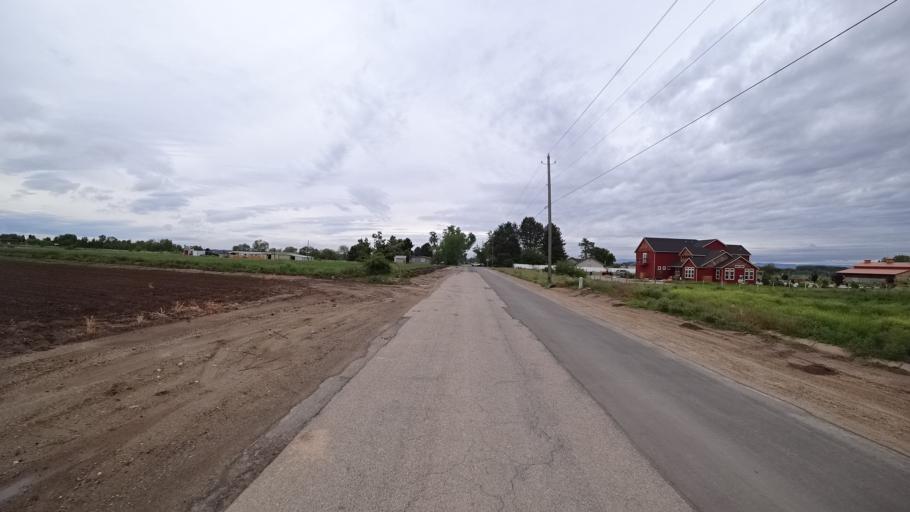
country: US
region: Idaho
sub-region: Ada County
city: Star
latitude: 43.7149
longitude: -116.4883
